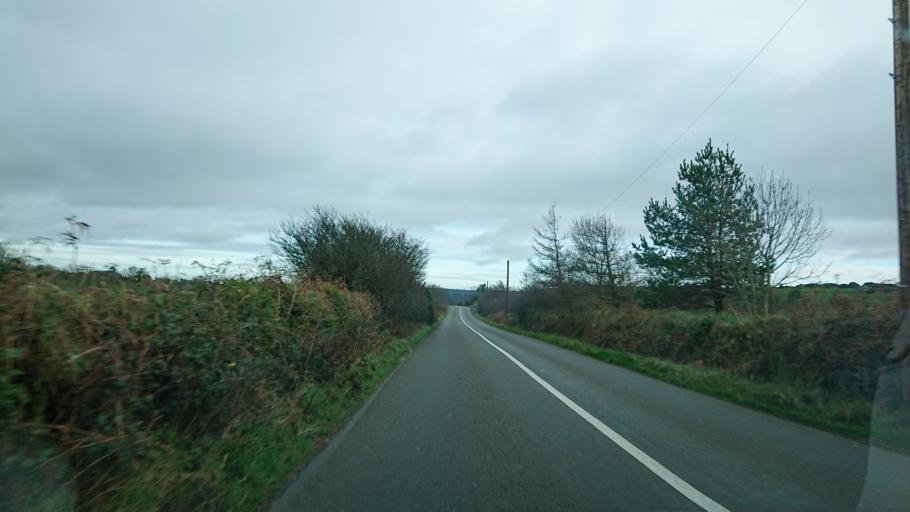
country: IE
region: Leinster
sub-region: Kilkenny
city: Mooncoin
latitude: 52.2043
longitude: -7.2617
